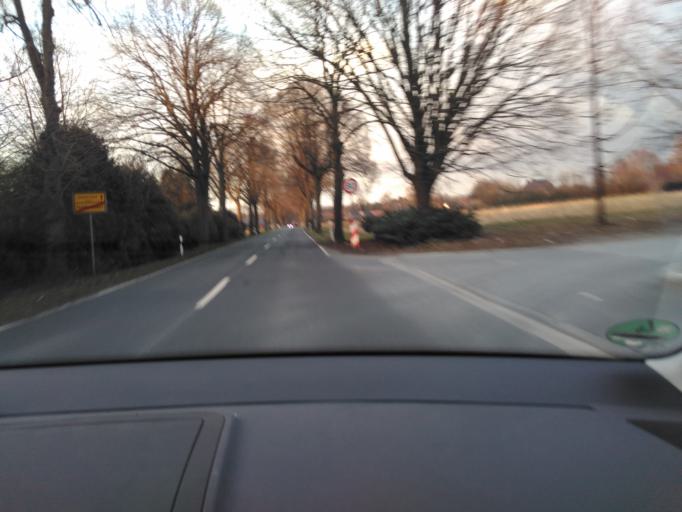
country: DE
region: North Rhine-Westphalia
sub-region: Regierungsbezirk Detmold
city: Verl
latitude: 51.9419
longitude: 8.4885
